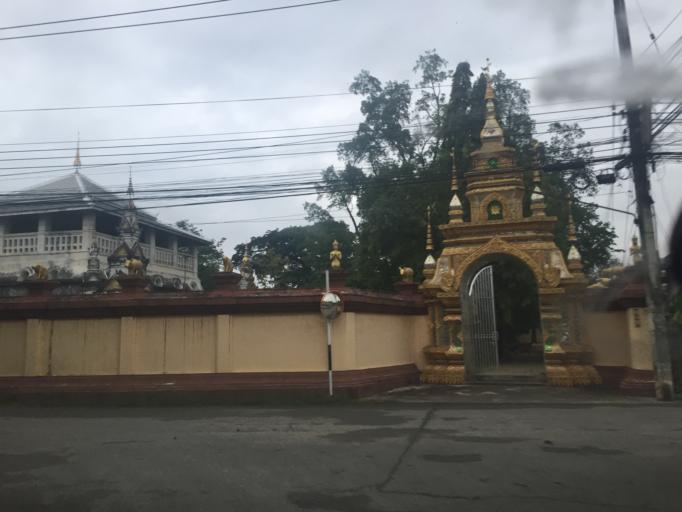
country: TH
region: Lamphun
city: Ban Thi
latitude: 18.6429
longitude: 99.0495
